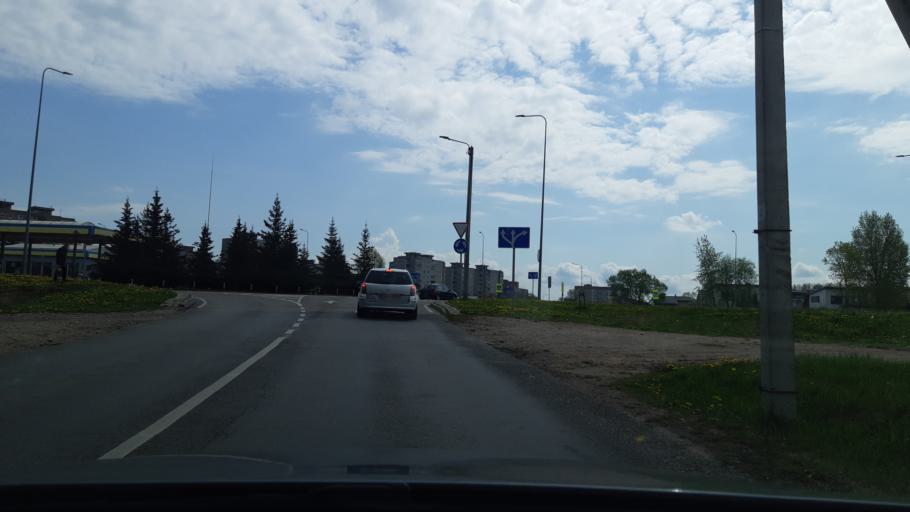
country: LT
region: Kauno apskritis
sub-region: Kaunas
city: Silainiai
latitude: 54.9229
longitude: 23.8685
